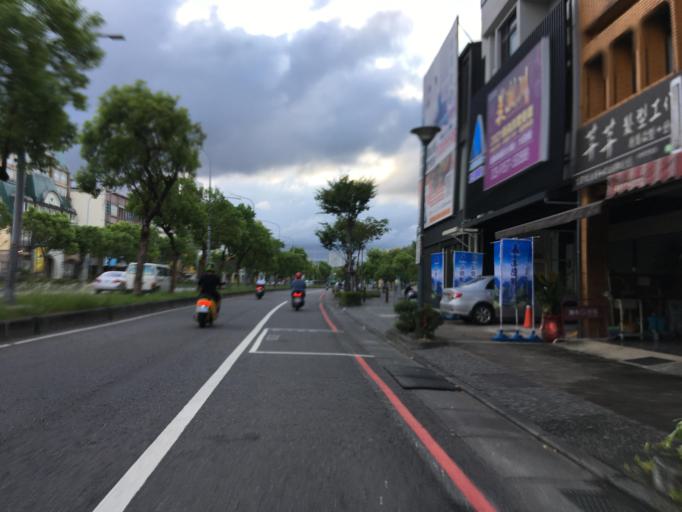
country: TW
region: Taiwan
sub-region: Yilan
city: Yilan
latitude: 24.6697
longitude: 121.7655
